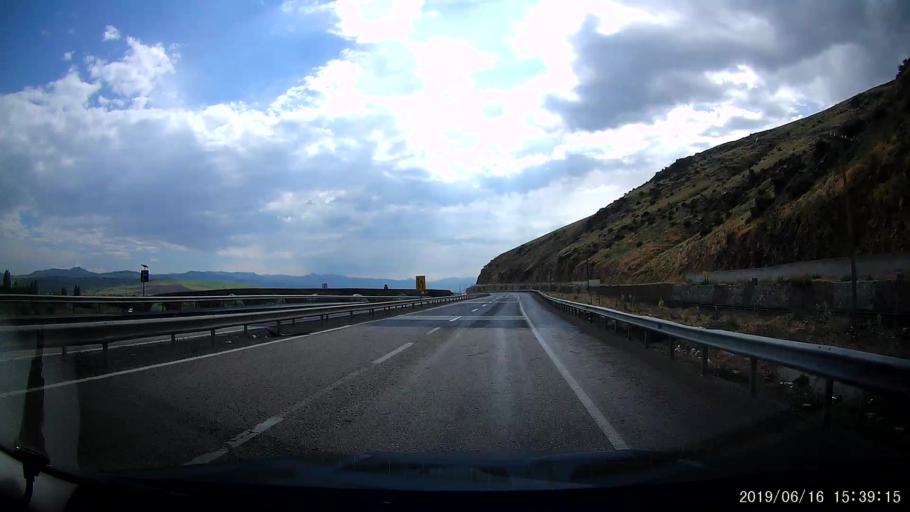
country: TR
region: Erzurum
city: Koprukoy
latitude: 39.9715
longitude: 41.8913
